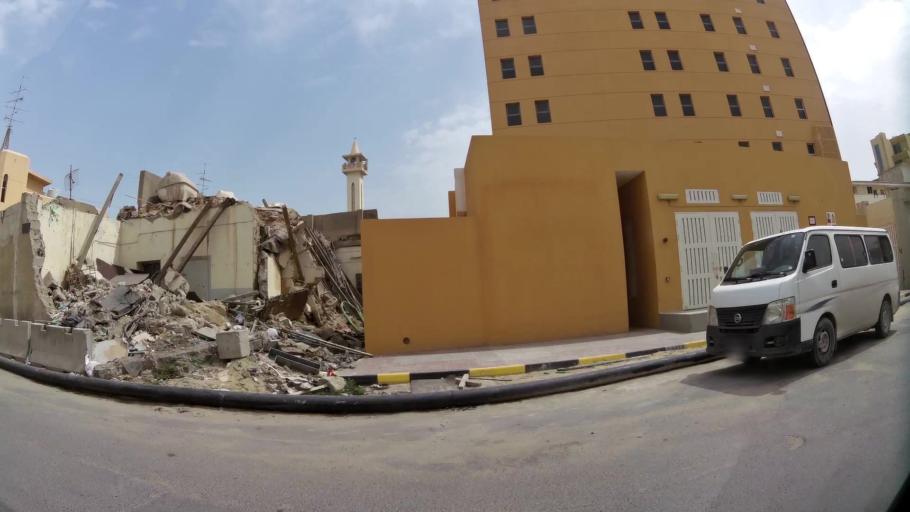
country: QA
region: Baladiyat ad Dawhah
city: Doha
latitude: 25.3042
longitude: 51.4985
